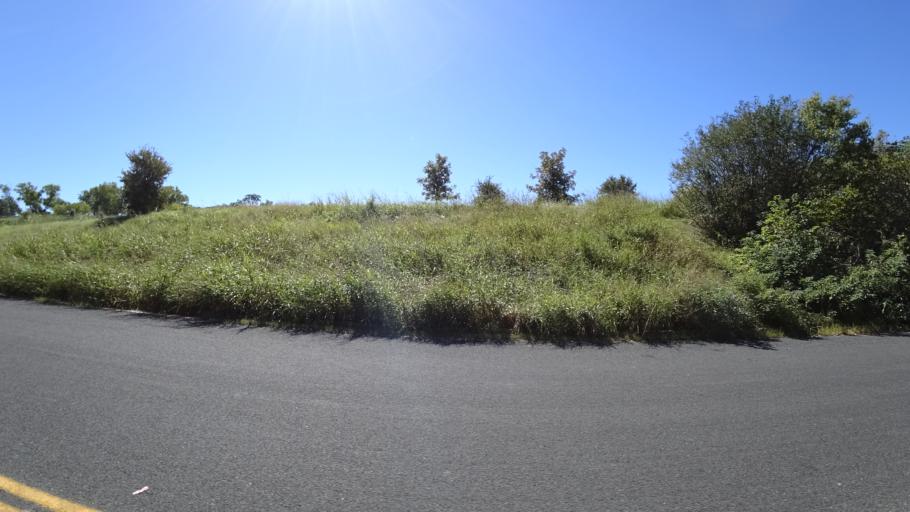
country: US
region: Texas
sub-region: Travis County
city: Austin
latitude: 30.2284
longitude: -97.7725
